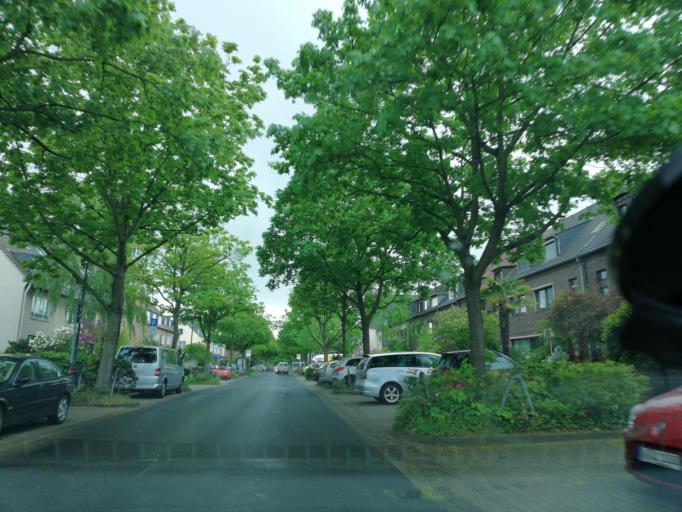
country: DE
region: North Rhine-Westphalia
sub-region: Regierungsbezirk Dusseldorf
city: Dusseldorf
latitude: 51.1990
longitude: 6.7629
